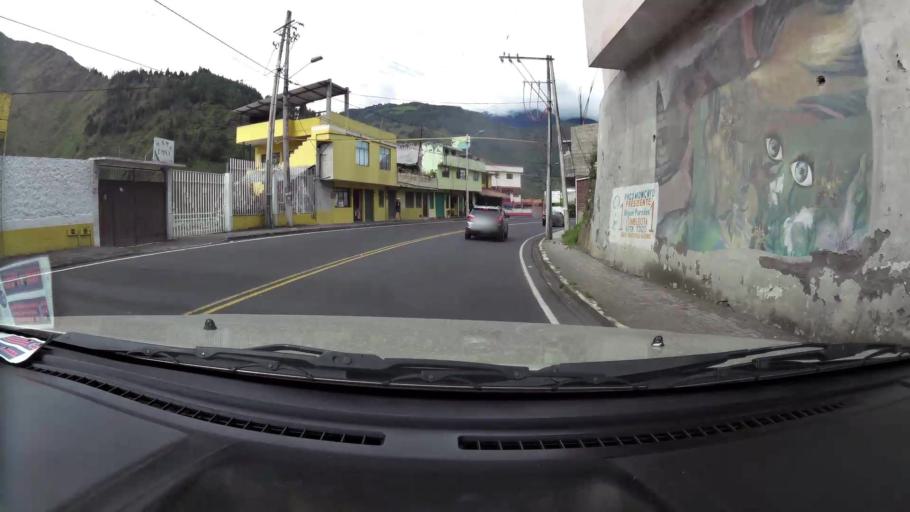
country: EC
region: Tungurahua
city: Banos
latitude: -1.3955
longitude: -78.4270
